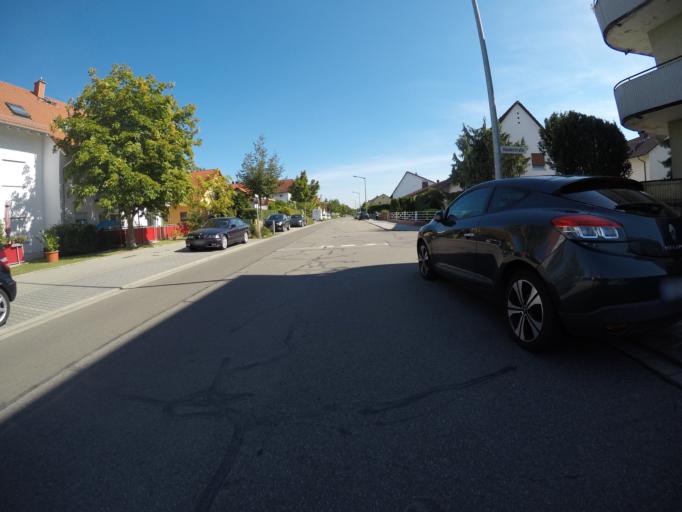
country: DE
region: Hesse
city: Lampertheim
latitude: 49.6053
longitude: 8.4710
